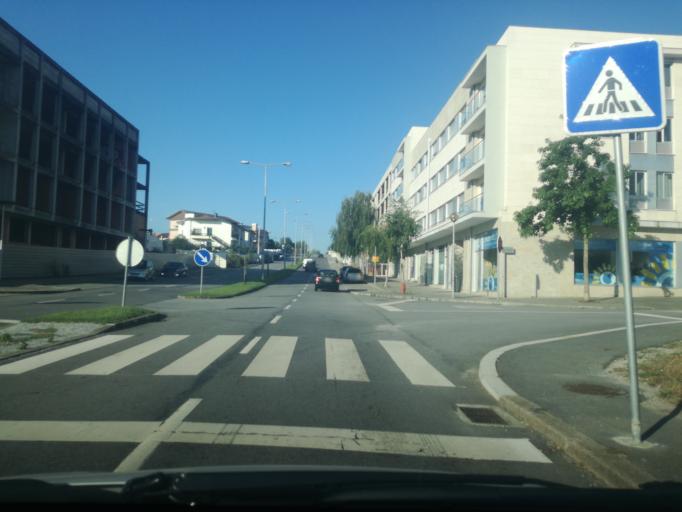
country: PT
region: Porto
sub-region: Maia
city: Leca do Bailio
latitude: 41.2152
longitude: -8.6077
